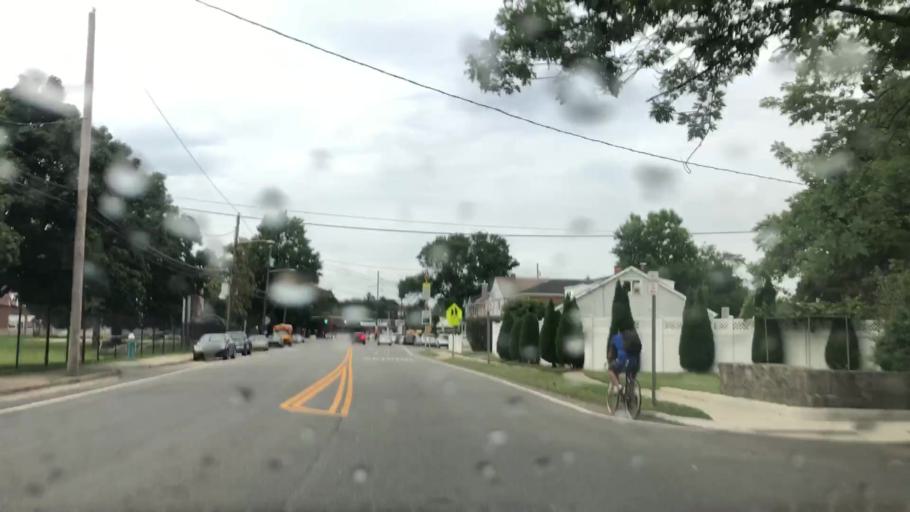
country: US
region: New York
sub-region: Nassau County
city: Stewart Manor
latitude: 40.7159
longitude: -73.6883
